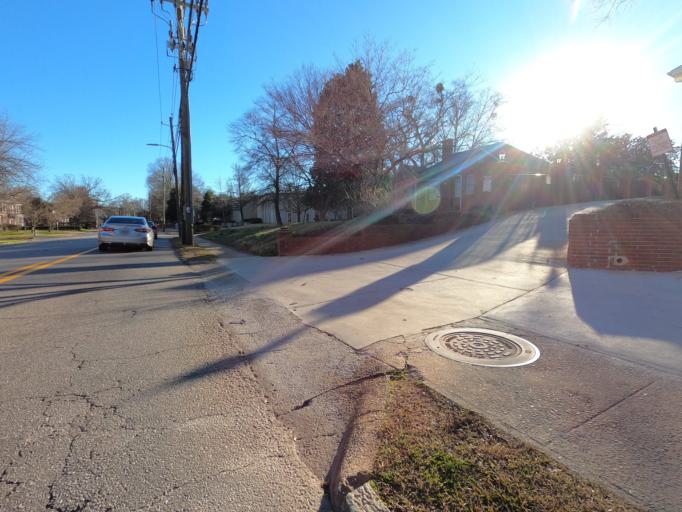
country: US
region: Georgia
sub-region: Clarke County
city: Athens
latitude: 33.9452
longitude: -83.3879
